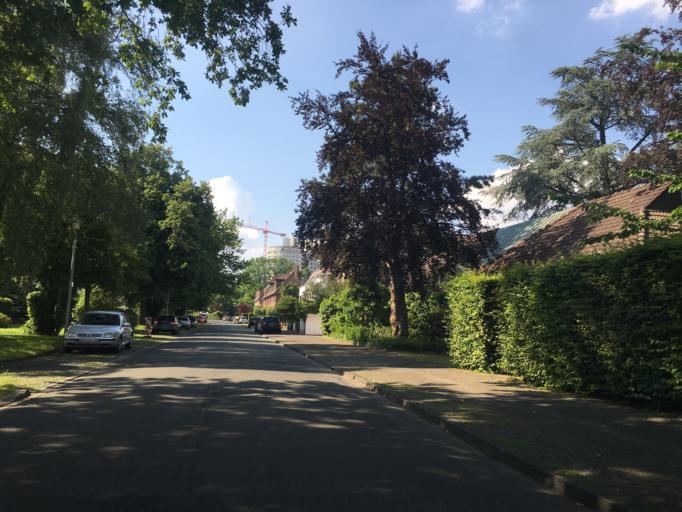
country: DE
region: North Rhine-Westphalia
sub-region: Regierungsbezirk Munster
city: Muenster
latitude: 51.9563
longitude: 7.5979
